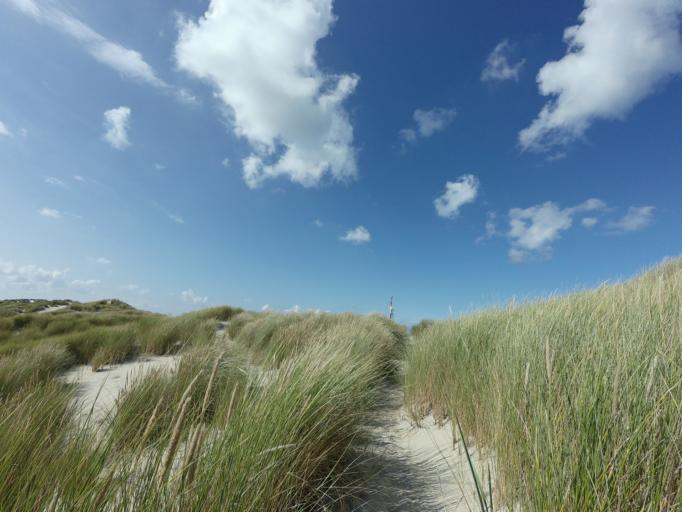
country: NL
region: Friesland
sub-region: Gemeente Terschelling
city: West-Terschelling
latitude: 53.3909
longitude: 5.2023
